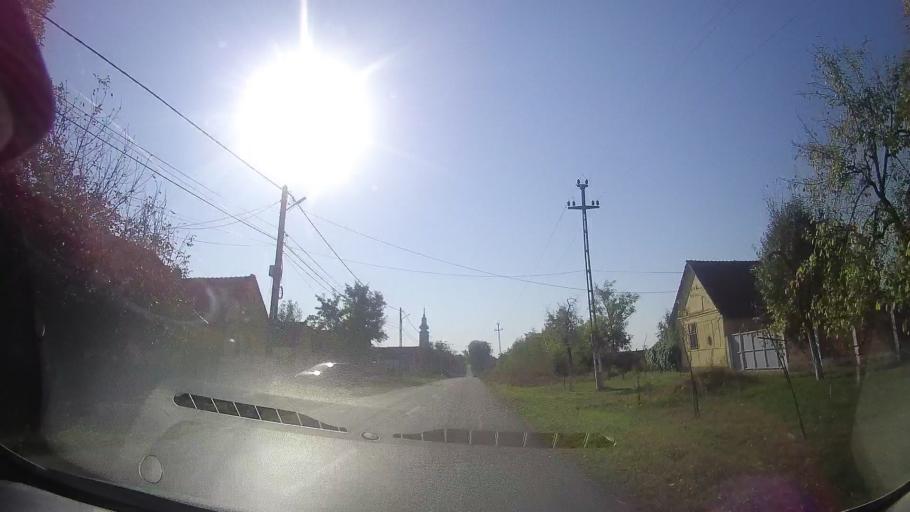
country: RO
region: Timis
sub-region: Comuna Topolovatu Mare
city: Topolovatu Mare
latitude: 45.8172
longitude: 21.5798
